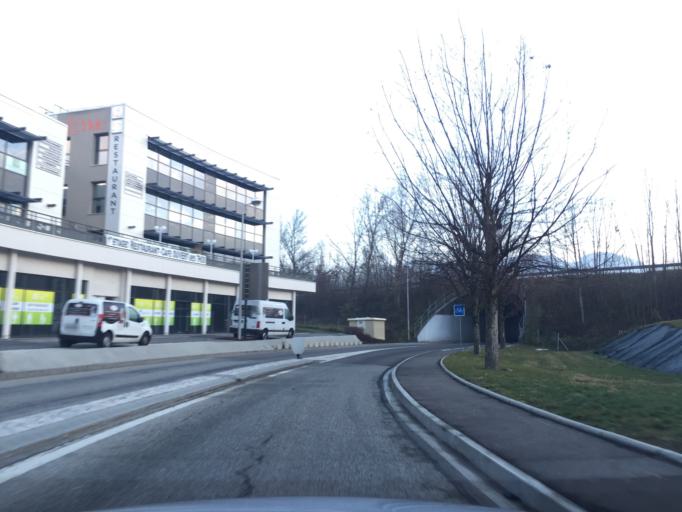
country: FR
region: Rhone-Alpes
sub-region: Departement de la Savoie
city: Gresy-sur-Aix
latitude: 45.7224
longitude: 5.9232
